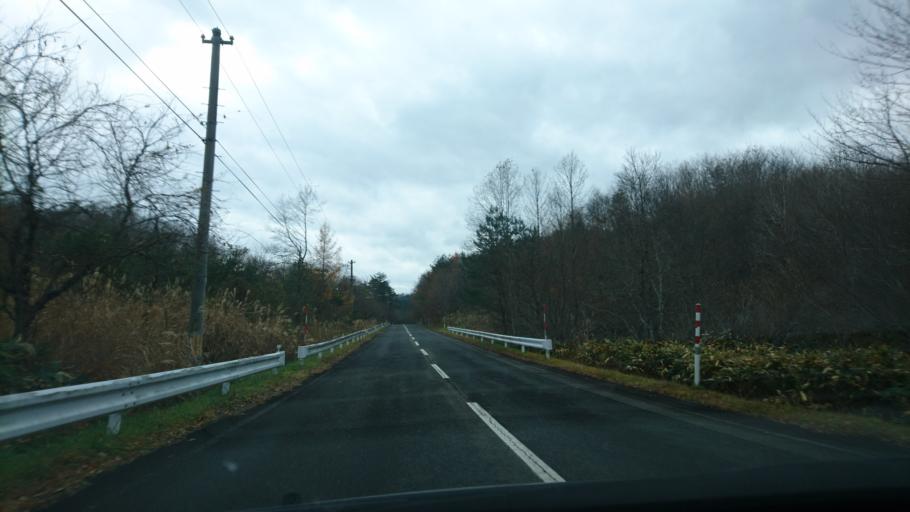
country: JP
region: Iwate
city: Ichinoseki
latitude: 38.9264
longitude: 140.9221
